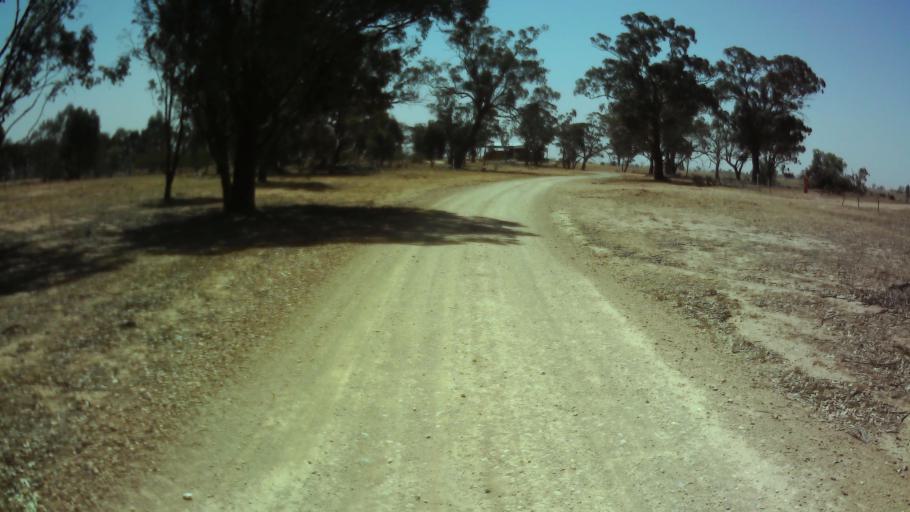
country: AU
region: New South Wales
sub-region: Weddin
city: Grenfell
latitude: -34.0157
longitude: 147.8975
